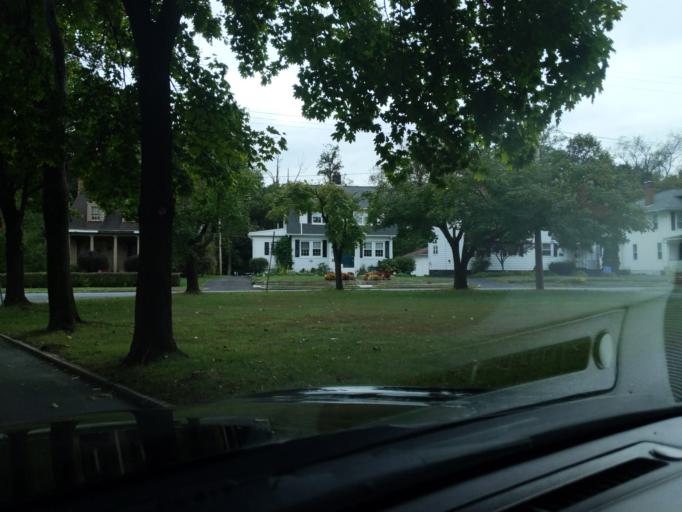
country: US
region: Pennsylvania
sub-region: Blair County
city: Lakemont
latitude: 40.4933
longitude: -78.4072
